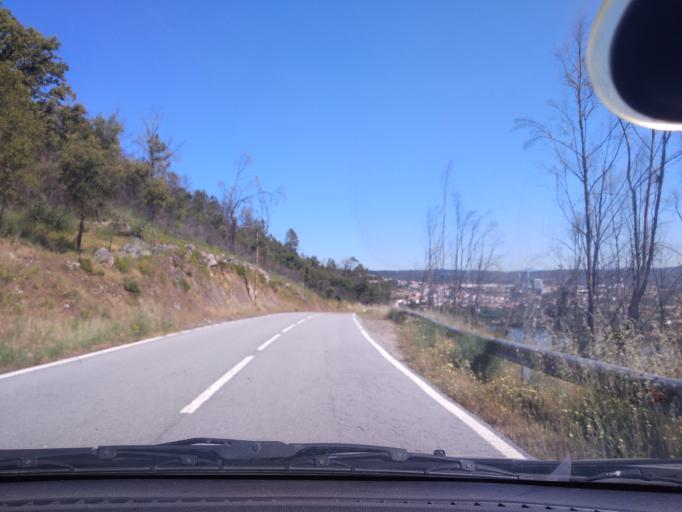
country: PT
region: Portalegre
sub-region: Nisa
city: Nisa
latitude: 39.6390
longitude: -7.6681
